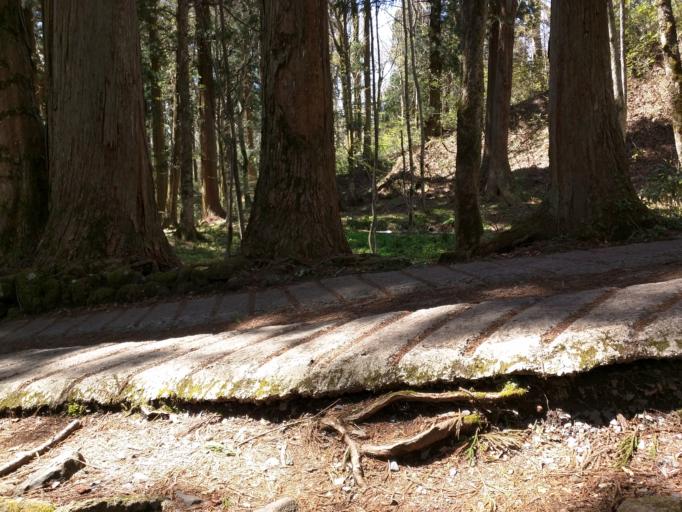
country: JP
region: Nagano
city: Nagano-shi
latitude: 36.7631
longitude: 138.0647
